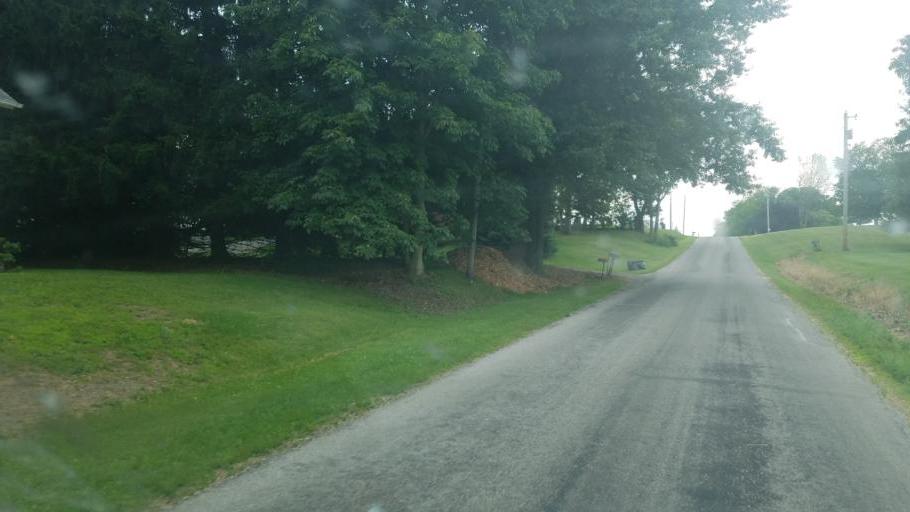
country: US
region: Ohio
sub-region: Wayne County
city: Shreve
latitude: 40.7775
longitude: -82.1181
